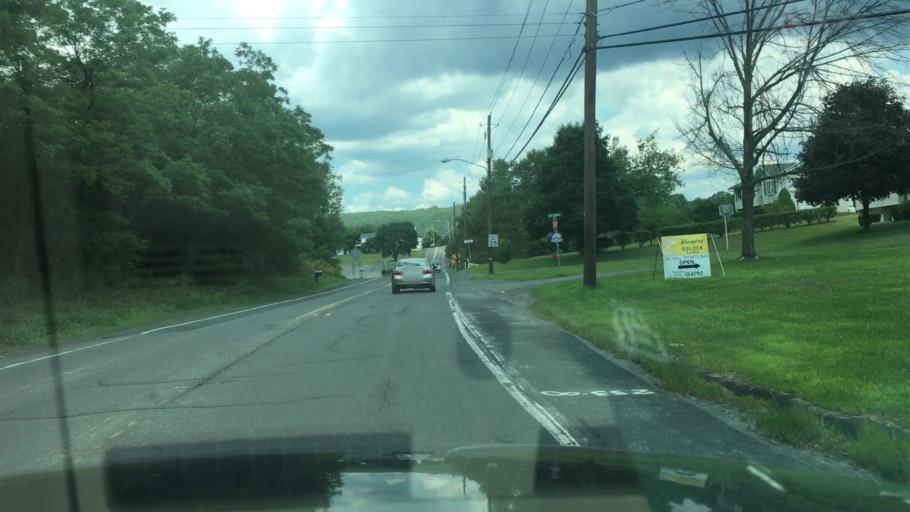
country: US
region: Pennsylvania
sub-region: Schuylkill County
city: Minersville
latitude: 40.6906
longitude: -76.2813
